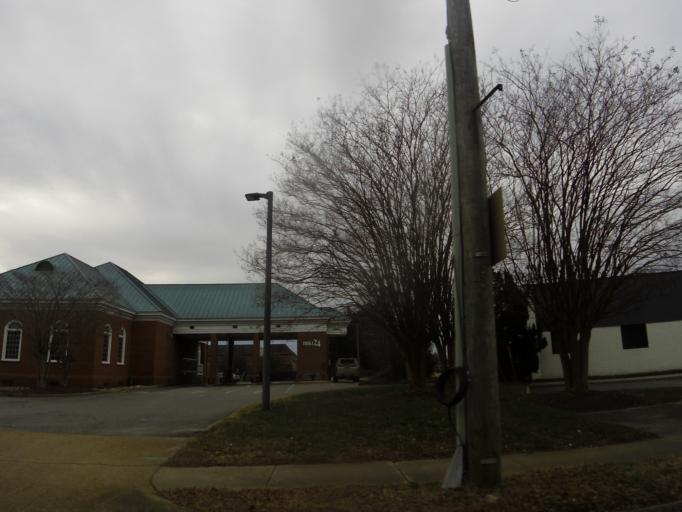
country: US
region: Virginia
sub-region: City of Portsmouth
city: Portsmouth Heights
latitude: 36.8343
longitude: -76.3425
